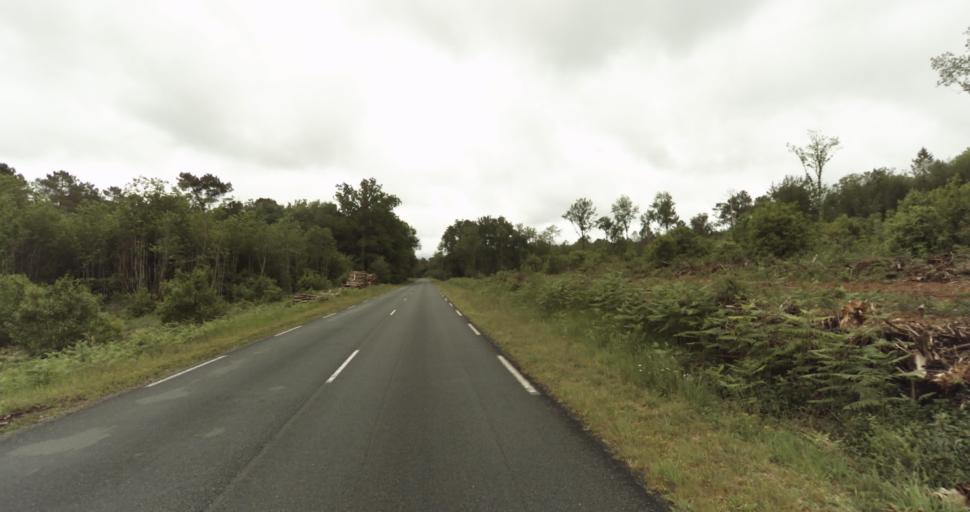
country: FR
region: Aquitaine
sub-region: Departement de la Dordogne
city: Belves
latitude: 44.6823
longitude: 0.9907
